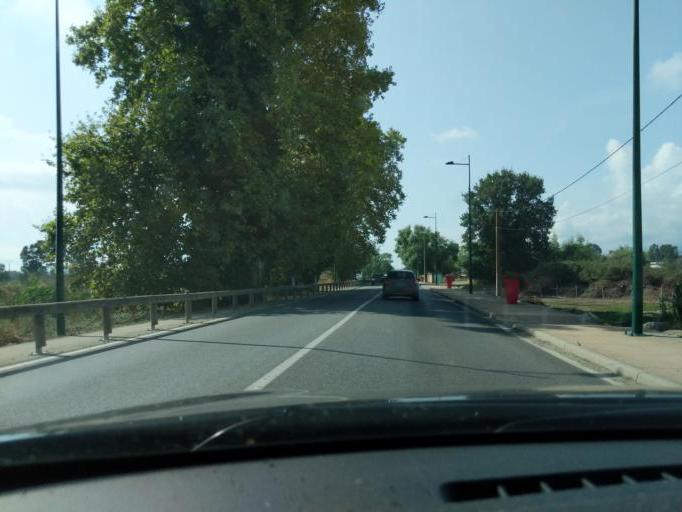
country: FR
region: Corsica
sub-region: Departement de la Haute-Corse
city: Ghisonaccia
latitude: 42.0055
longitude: 9.4032
